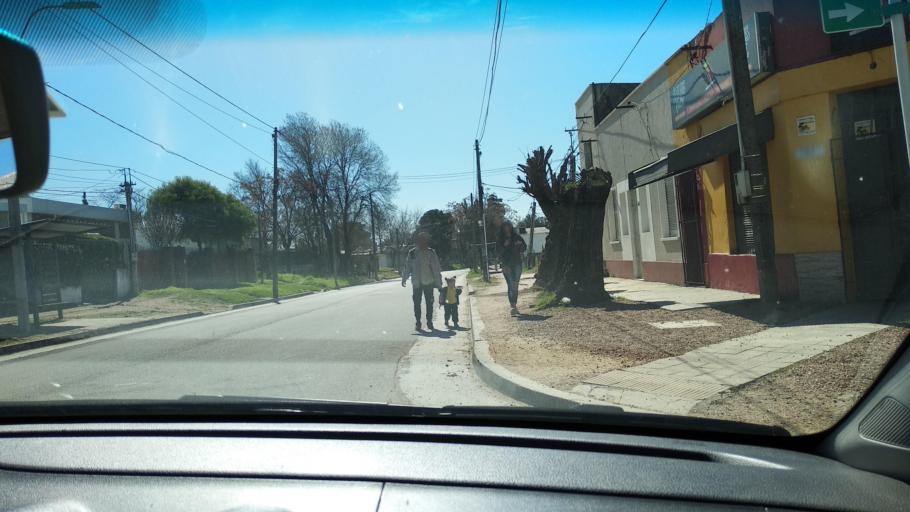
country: UY
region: Canelones
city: Las Piedras
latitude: -34.7241
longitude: -56.2100
